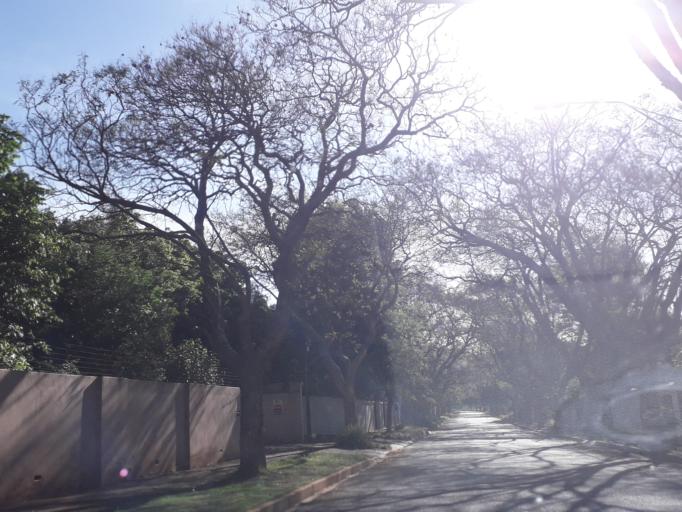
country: ZA
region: Gauteng
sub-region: City of Johannesburg Metropolitan Municipality
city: Johannesburg
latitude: -26.1619
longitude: 28.0085
